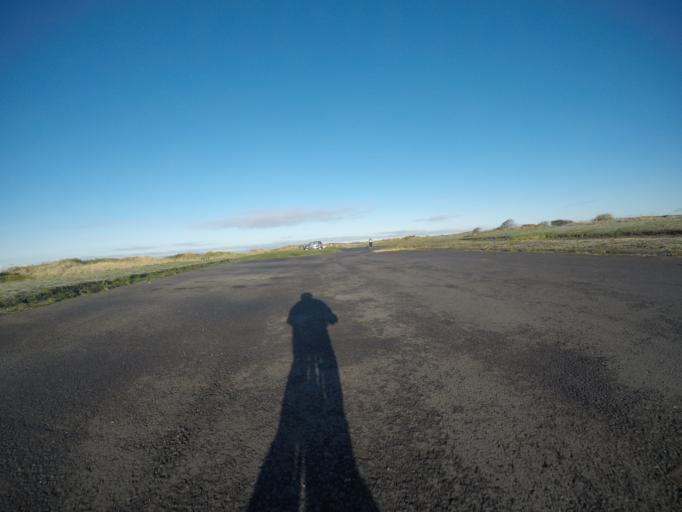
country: GB
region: Scotland
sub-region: North Ayrshire
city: Stevenston
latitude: 55.6305
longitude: -4.7532
